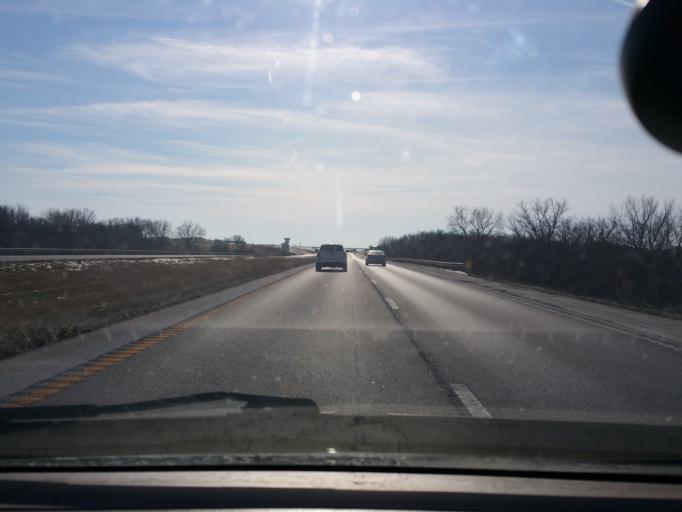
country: US
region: Missouri
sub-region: Clinton County
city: Cameron
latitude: 39.7404
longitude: -94.2204
